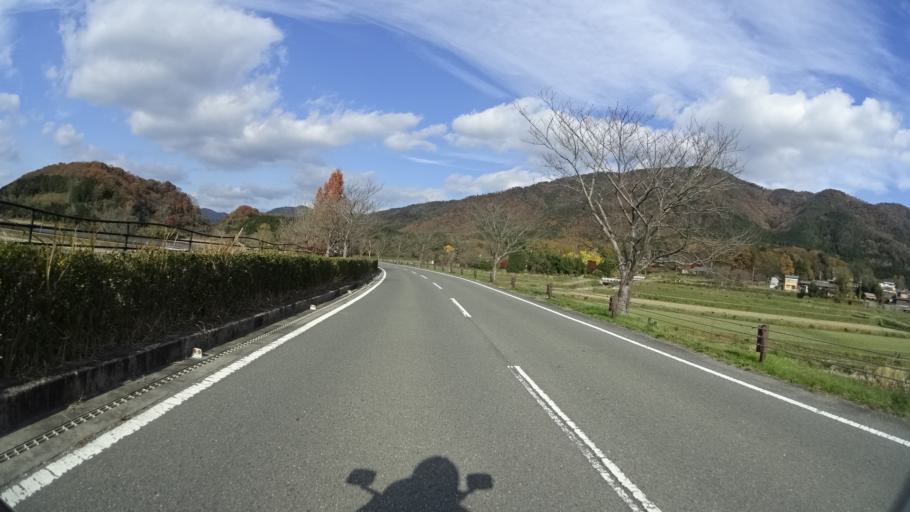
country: JP
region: Kyoto
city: Kameoka
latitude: 35.0657
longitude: 135.5671
